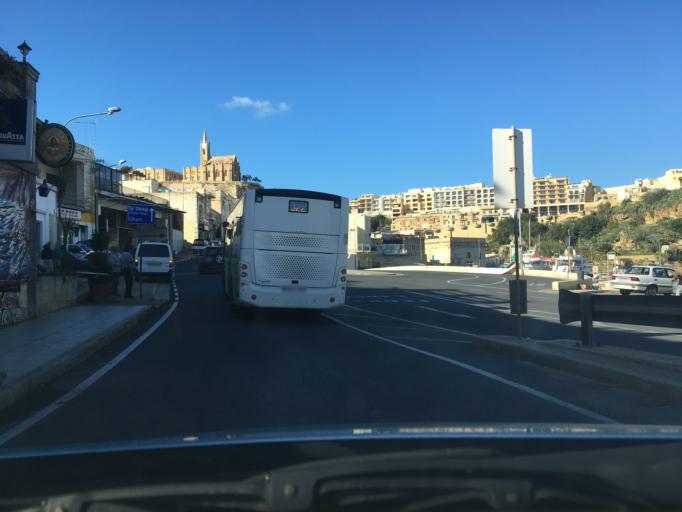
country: MT
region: Ghajnsielem
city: Mgarr
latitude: 36.0237
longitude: 14.2975
